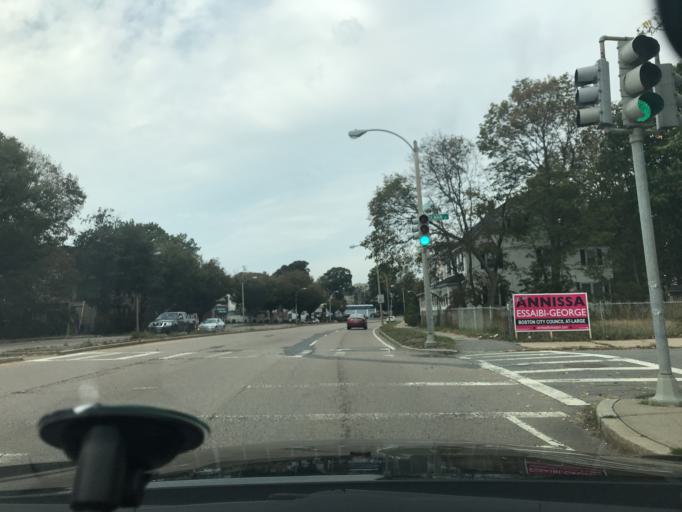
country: US
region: Massachusetts
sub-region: Suffolk County
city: South Boston
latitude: 42.2899
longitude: -71.0452
